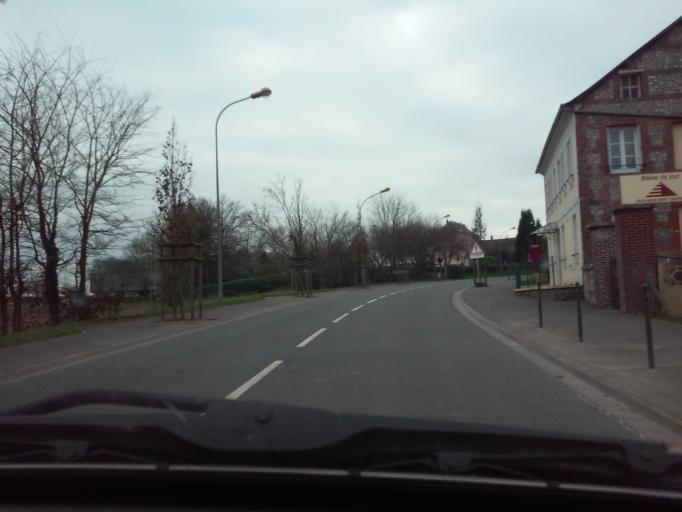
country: FR
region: Haute-Normandie
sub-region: Departement de la Seine-Maritime
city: Saint-Arnoult
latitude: 49.5280
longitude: 0.6701
